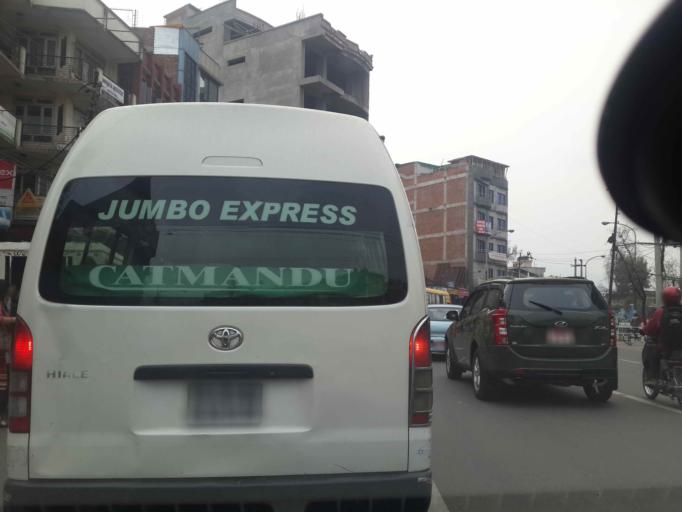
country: NP
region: Central Region
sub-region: Bagmati Zone
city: Patan
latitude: 27.6878
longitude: 85.3165
